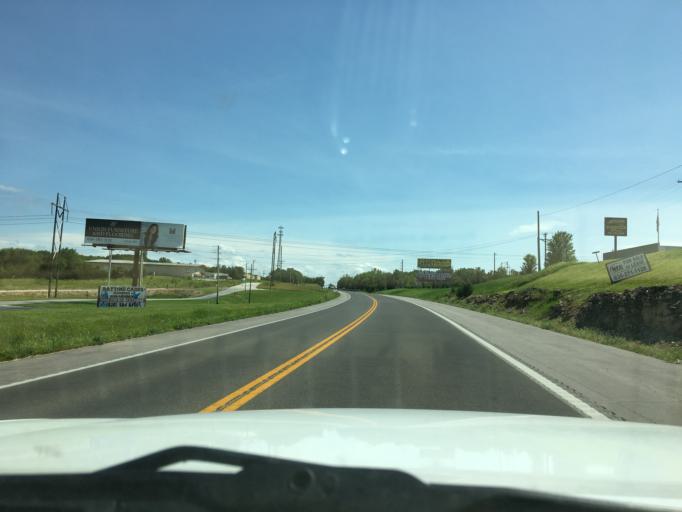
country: US
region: Missouri
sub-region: Franklin County
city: Union
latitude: 38.4905
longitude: -91.0052
